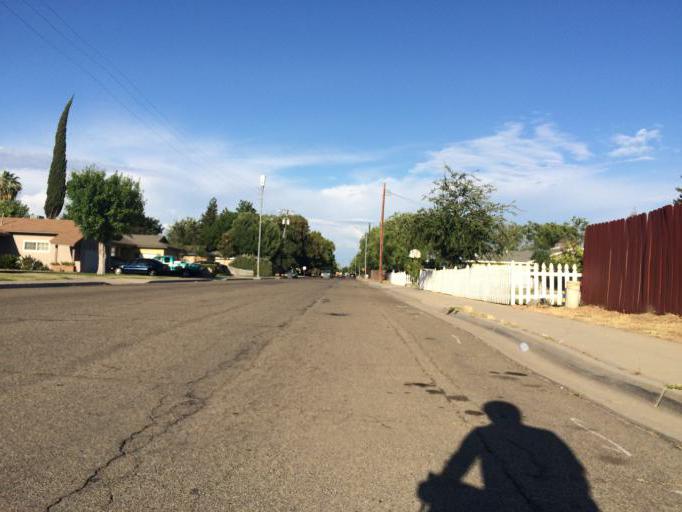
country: US
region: California
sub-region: Fresno County
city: Tarpey Village
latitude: 36.7976
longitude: -119.7243
